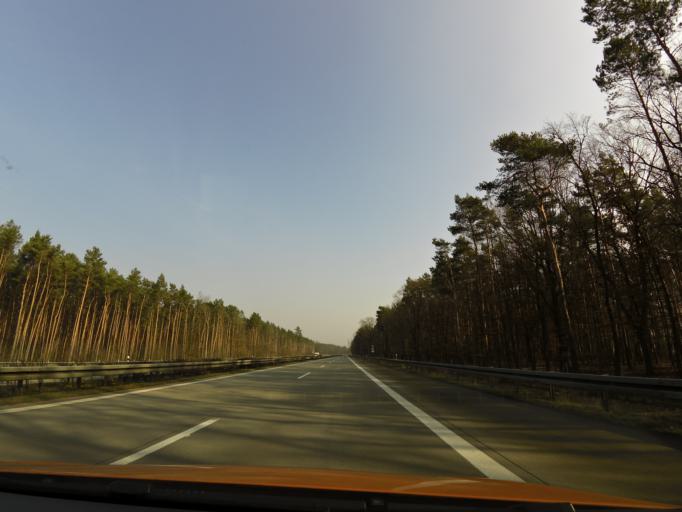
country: DE
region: Brandenburg
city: Berkenbruck
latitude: 52.3405
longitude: 14.1646
